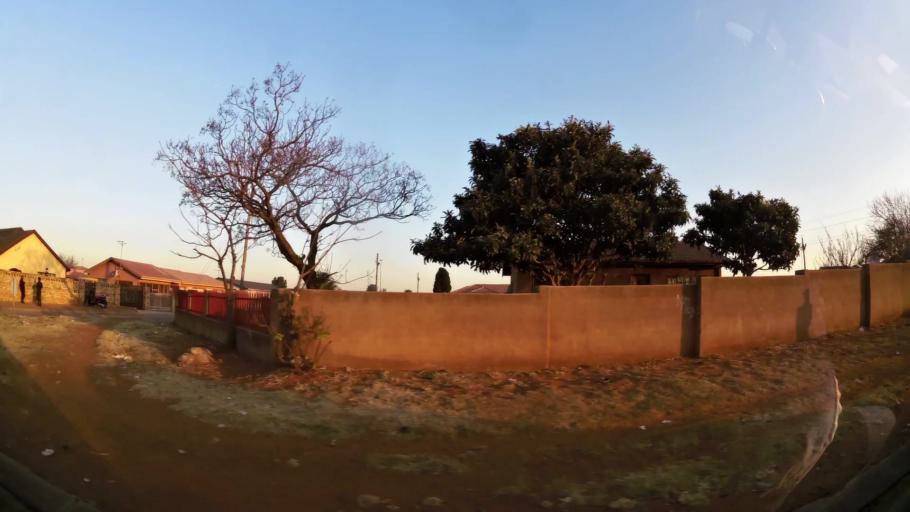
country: ZA
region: Gauteng
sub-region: West Rand District Municipality
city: Randfontein
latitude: -26.2018
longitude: 27.7083
